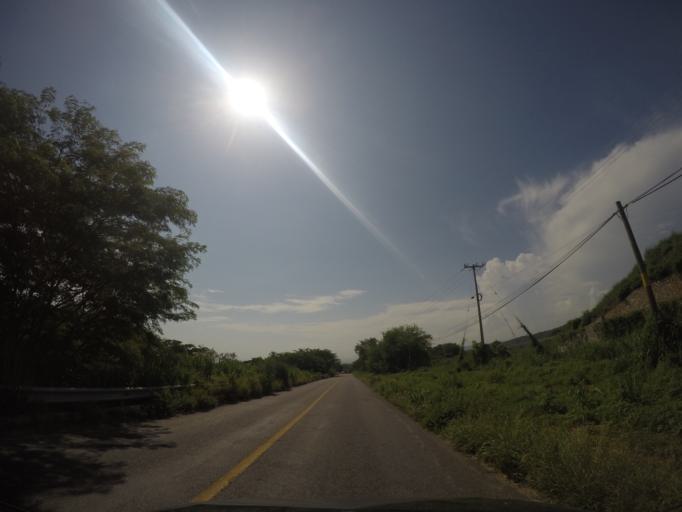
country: MX
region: Oaxaca
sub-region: San Pedro Mixtepec -Dto. 22 -
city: Puerto Escondido
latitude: 15.8766
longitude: -97.1005
